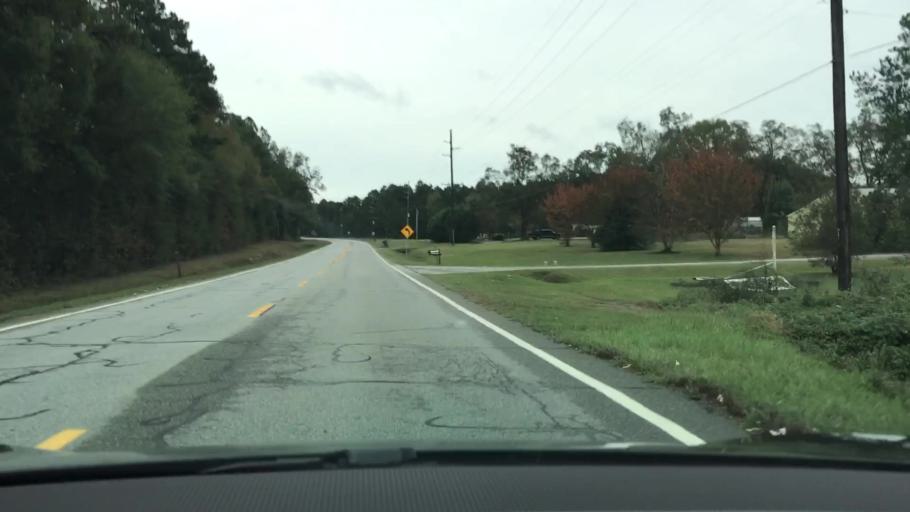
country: US
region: Georgia
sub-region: Warren County
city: Warrenton
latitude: 33.3950
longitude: -82.6510
